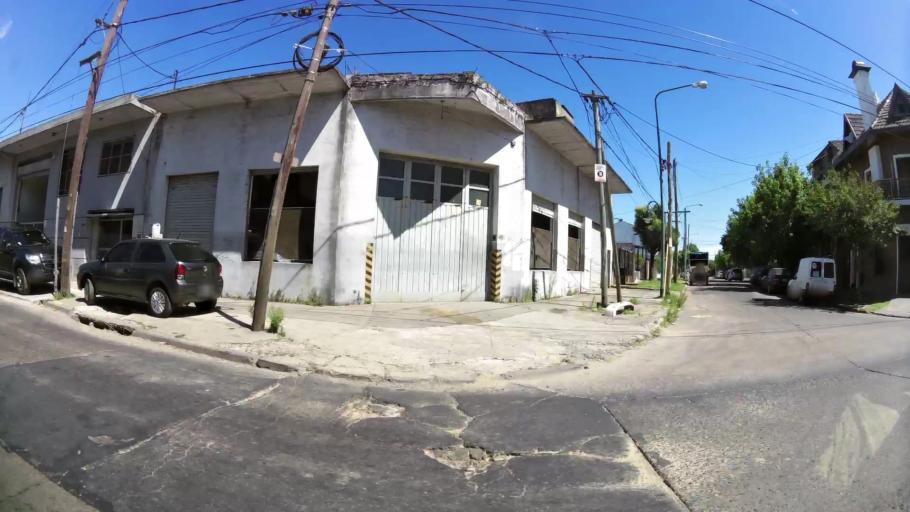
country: AR
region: Buenos Aires
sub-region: Partido de General San Martin
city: General San Martin
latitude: -34.5438
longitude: -58.5374
